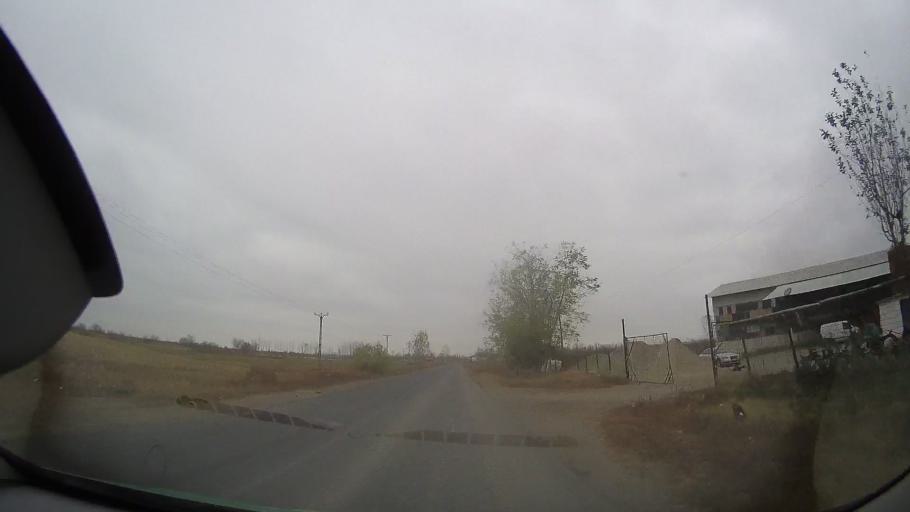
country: RO
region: Braila
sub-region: Comuna Ciocile
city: Ciocile
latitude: 44.8173
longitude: 27.2581
